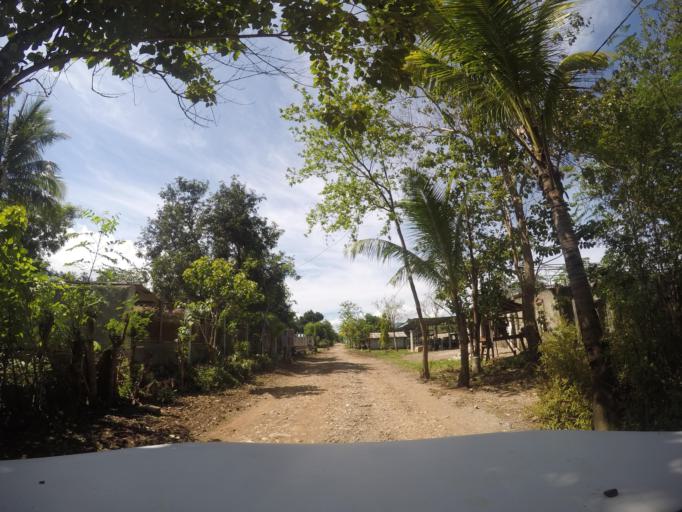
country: TL
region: Bobonaro
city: Maliana
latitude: -8.9880
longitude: 125.1992
